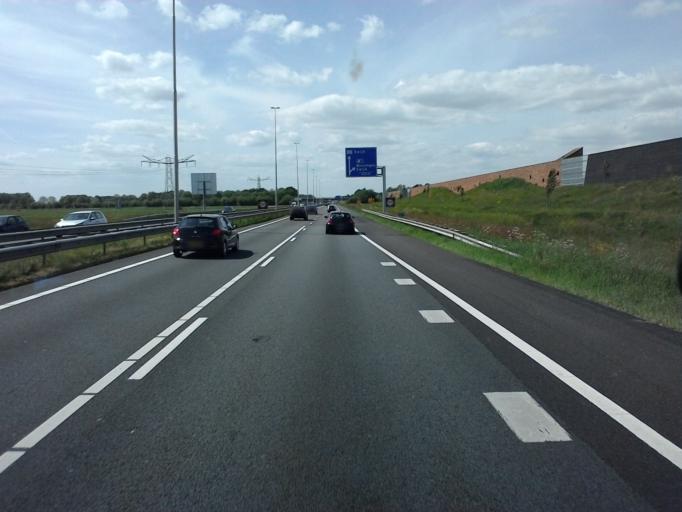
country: NL
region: Gelderland
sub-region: Gemeente Beuningen
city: Beuningen
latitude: 51.8463
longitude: 5.7655
